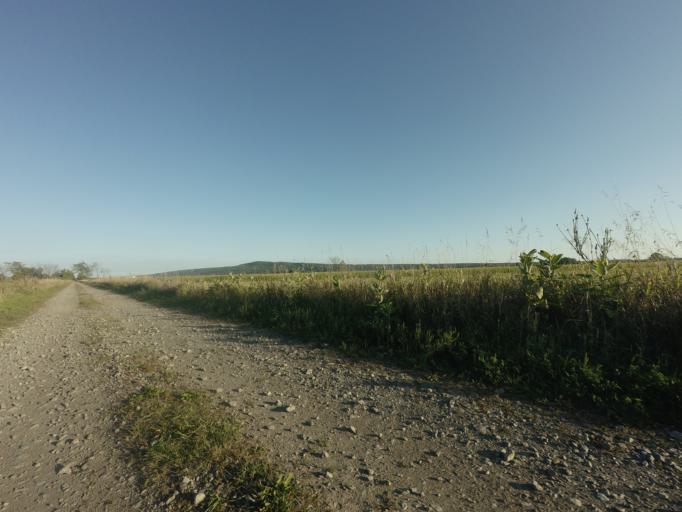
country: CA
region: Quebec
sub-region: Monteregie
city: Rigaud
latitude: 45.4861
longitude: -74.3602
